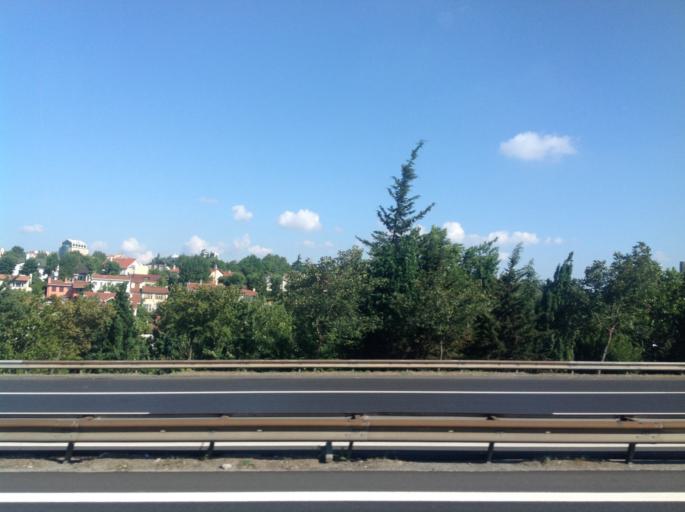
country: TR
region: Istanbul
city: Sisli
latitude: 41.0858
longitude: 29.0135
